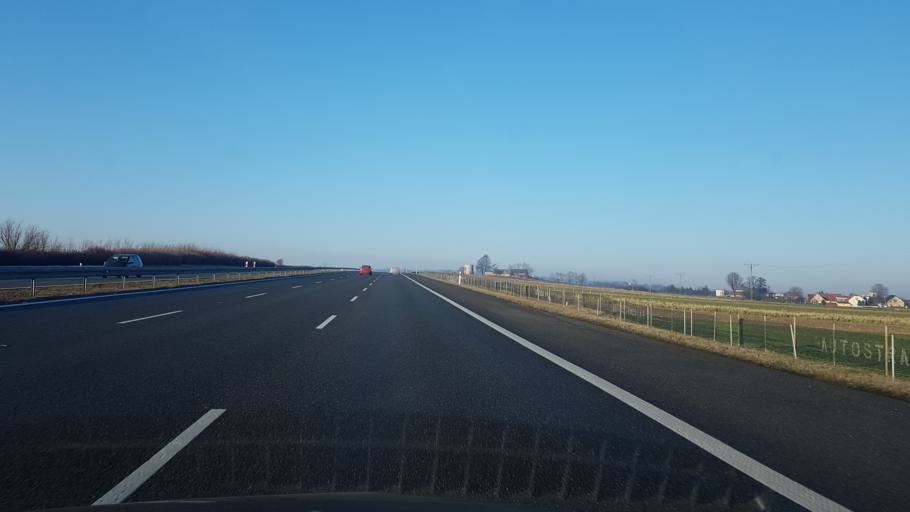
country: PL
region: Opole Voivodeship
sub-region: Powiat strzelecki
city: Lesnica
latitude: 50.4667
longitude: 18.2031
